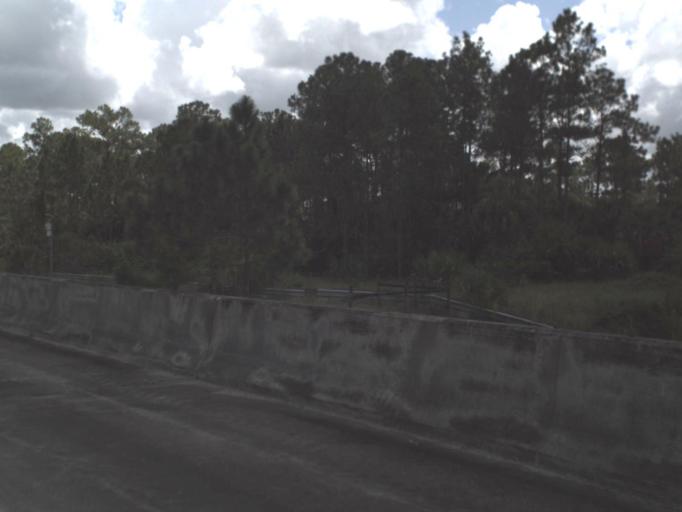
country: US
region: Florida
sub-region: Collier County
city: Orangetree
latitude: 26.1528
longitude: -81.5552
